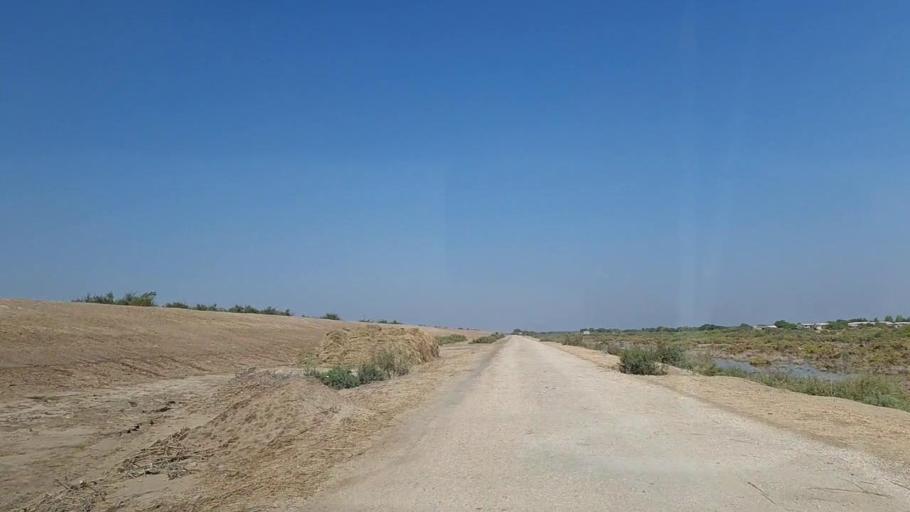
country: PK
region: Sindh
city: Chuhar Jamali
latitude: 24.4564
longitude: 68.0002
